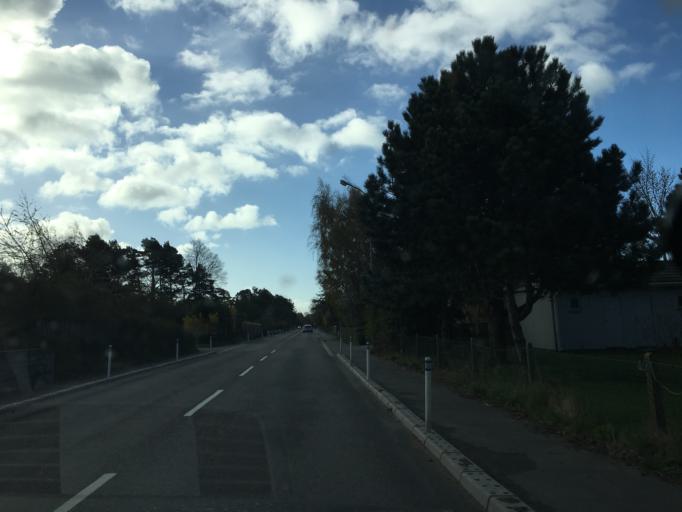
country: SE
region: Skane
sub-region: Vellinge Kommun
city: Hollviken
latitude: 55.4158
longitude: 12.9511
